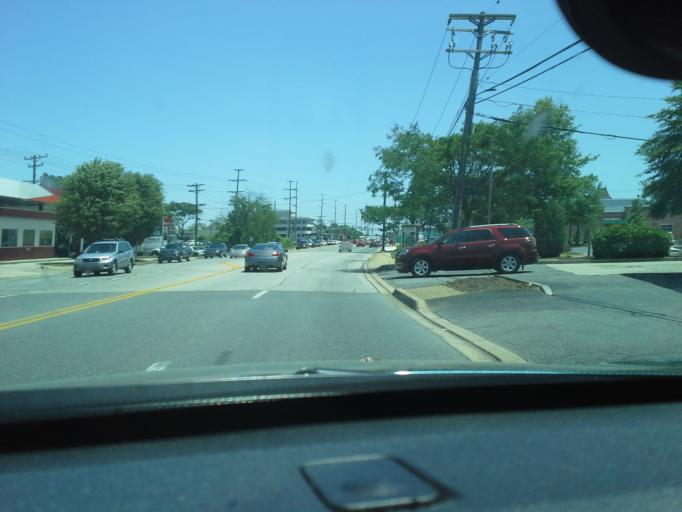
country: US
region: Maryland
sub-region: Anne Arundel County
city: Parole
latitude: 38.9823
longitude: -76.5392
